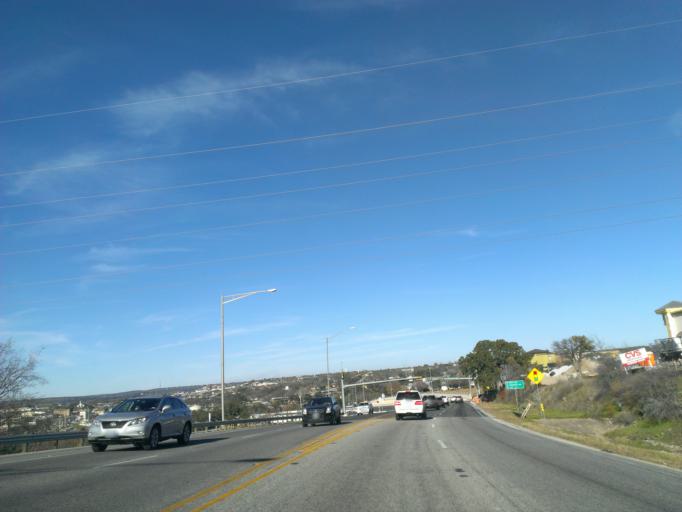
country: US
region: Texas
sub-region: Burnet County
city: Marble Falls
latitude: 30.5621
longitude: -98.2758
